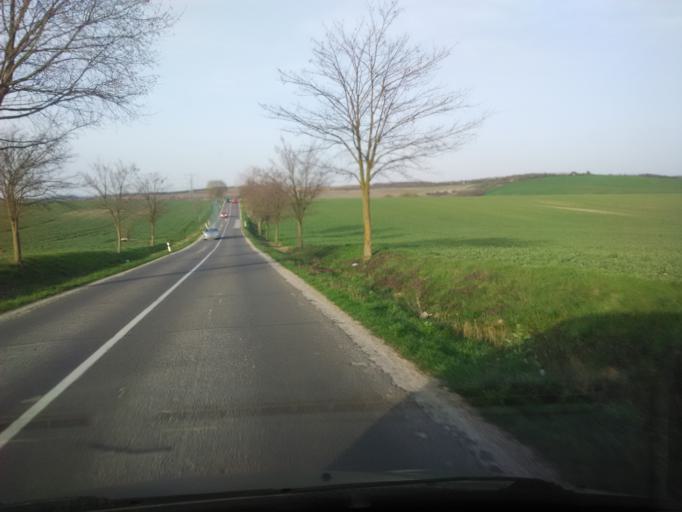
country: SK
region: Nitriansky
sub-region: Okres Nitra
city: Vrable
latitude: 48.1206
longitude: 18.3850
